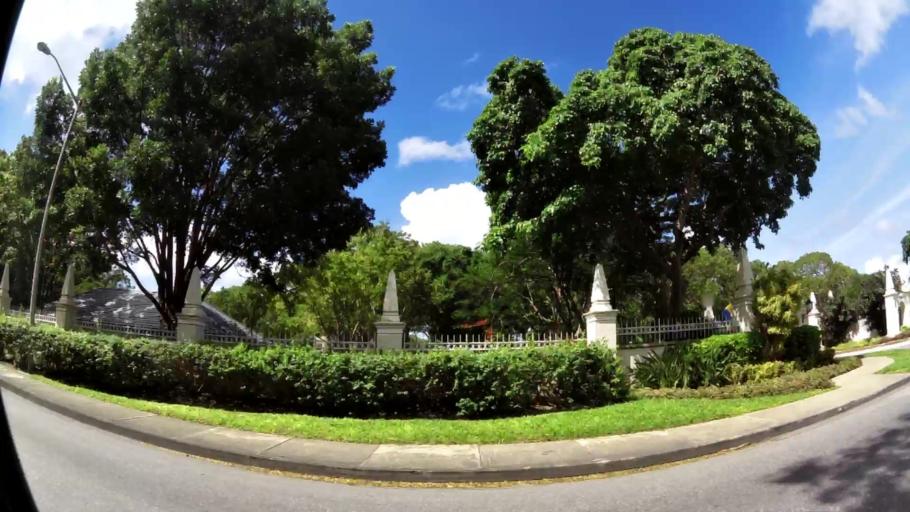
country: BB
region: Saint James
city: Holetown
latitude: 13.1728
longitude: -59.6357
